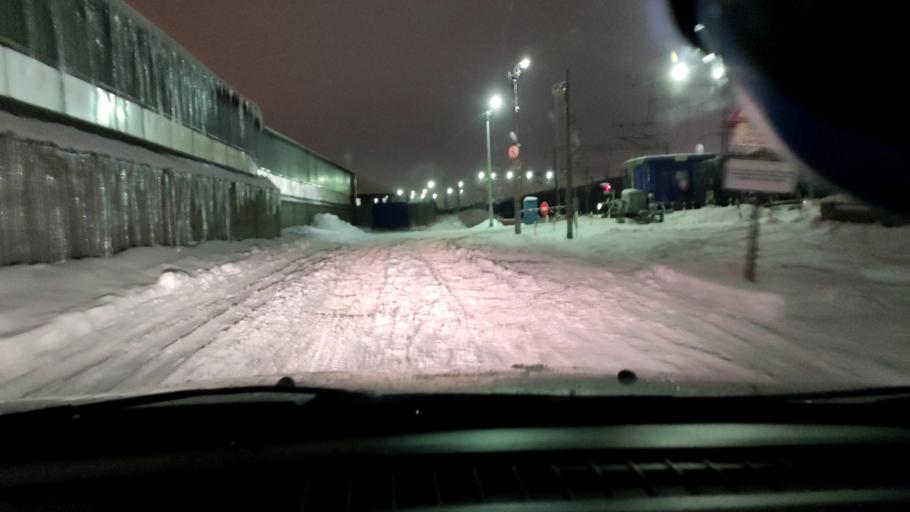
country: RU
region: Perm
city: Kondratovo
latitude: 58.0376
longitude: 56.1105
